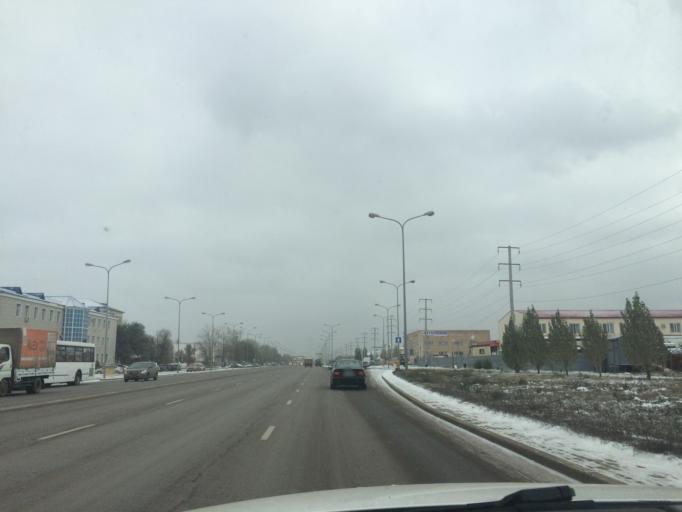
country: KZ
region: Astana Qalasy
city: Astana
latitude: 51.1819
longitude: 71.4586
